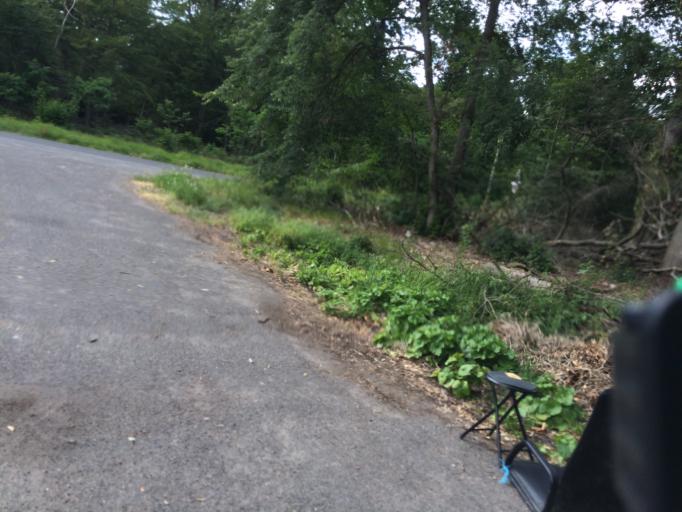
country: FR
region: Ile-de-France
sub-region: Departement de l'Essonne
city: Soisy-sur-Seine
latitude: 48.6668
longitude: 2.4346
